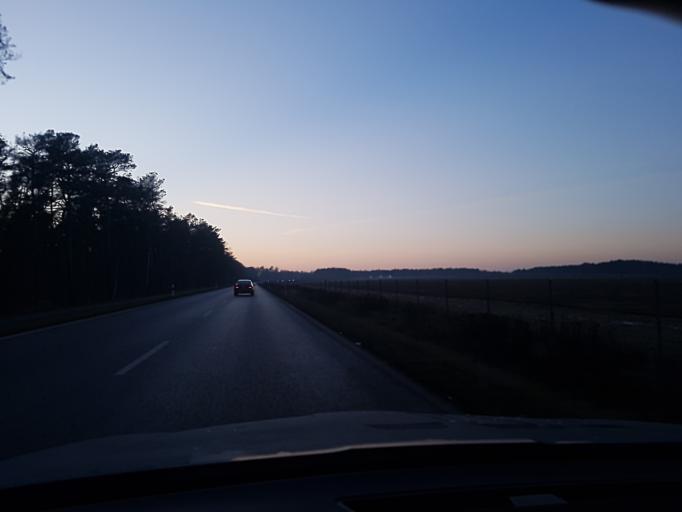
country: DE
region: Brandenburg
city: Finsterwalde
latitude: 51.6333
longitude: 13.6764
